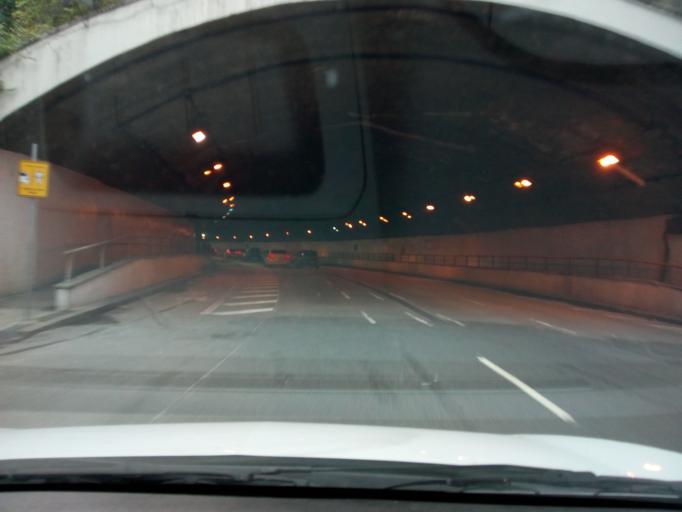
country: BR
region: Rio de Janeiro
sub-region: Rio De Janeiro
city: Rio de Janeiro
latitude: -22.9697
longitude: -43.1900
